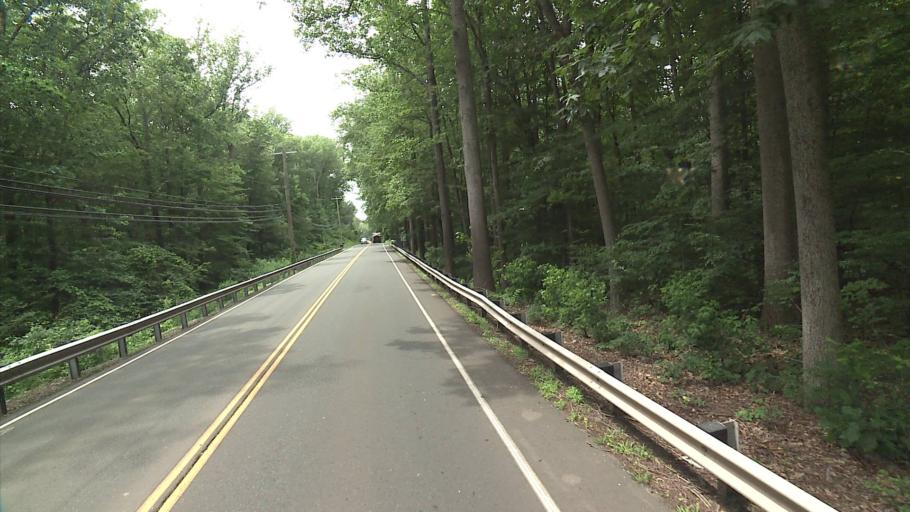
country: US
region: Connecticut
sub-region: New Haven County
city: Madison Center
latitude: 41.3591
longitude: -72.6250
